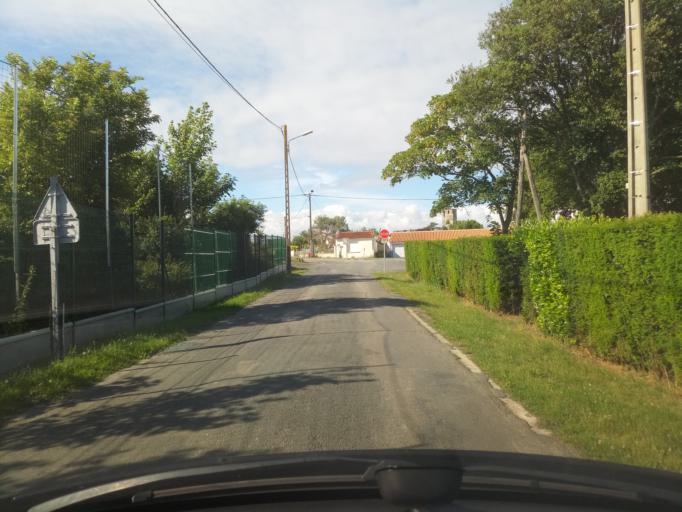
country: FR
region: Poitou-Charentes
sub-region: Departement de la Charente-Maritime
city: Marans
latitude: 46.3031
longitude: -0.9940
